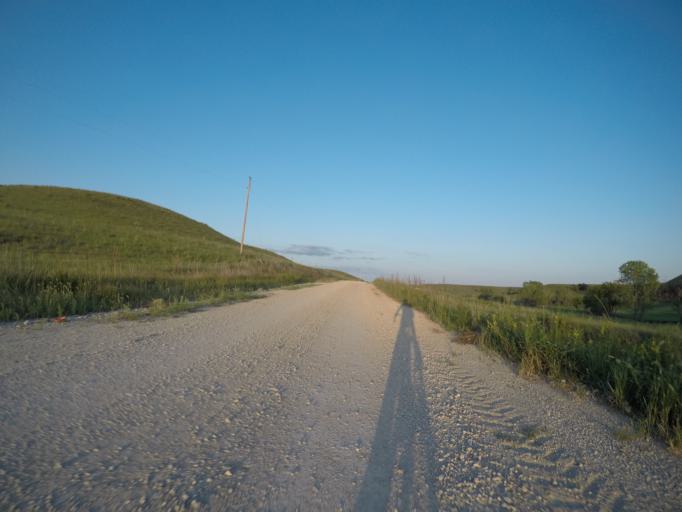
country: US
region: Kansas
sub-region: Riley County
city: Ogden
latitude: 39.0057
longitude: -96.6223
